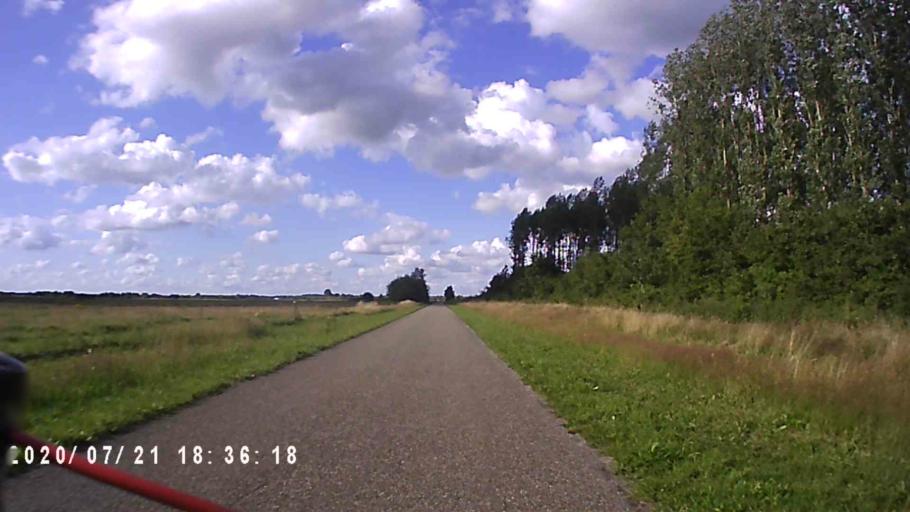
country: NL
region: Groningen
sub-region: Gemeente Hoogezand-Sappemeer
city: Hoogezand
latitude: 53.1932
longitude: 6.7414
